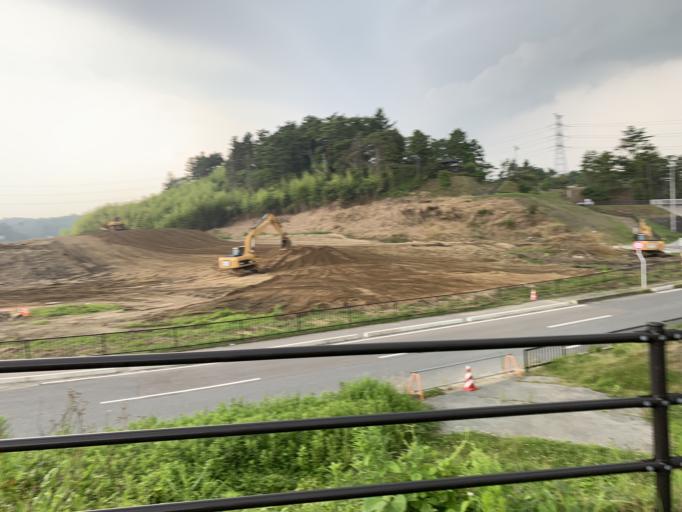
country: JP
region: Fukushima
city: Namie
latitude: 37.6578
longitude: 141.0180
